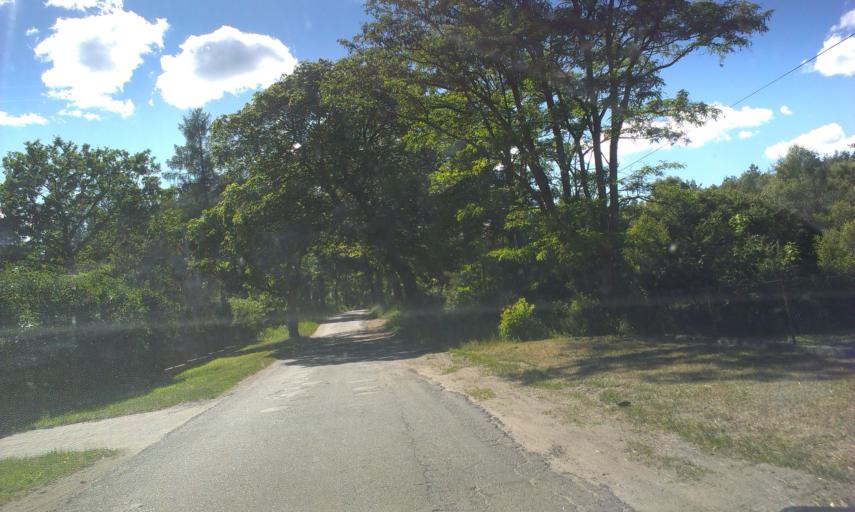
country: PL
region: West Pomeranian Voivodeship
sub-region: Powiat szczecinecki
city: Szczecinek
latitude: 53.8015
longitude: 16.6836
